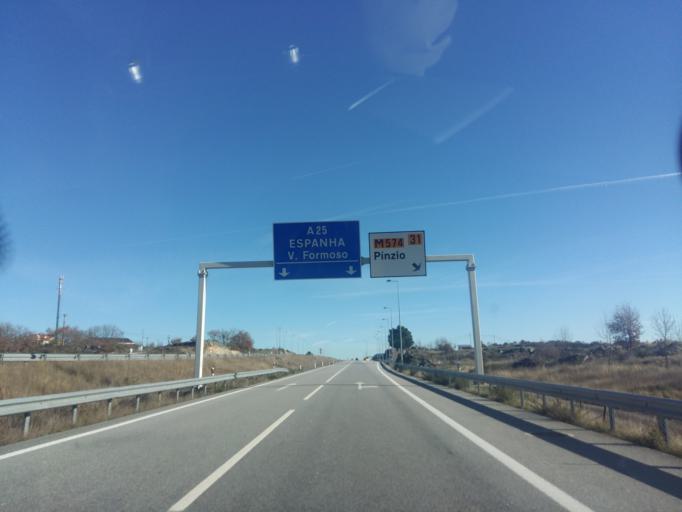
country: PT
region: Guarda
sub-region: Guarda
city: Sequeira
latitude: 40.6054
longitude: -7.0731
